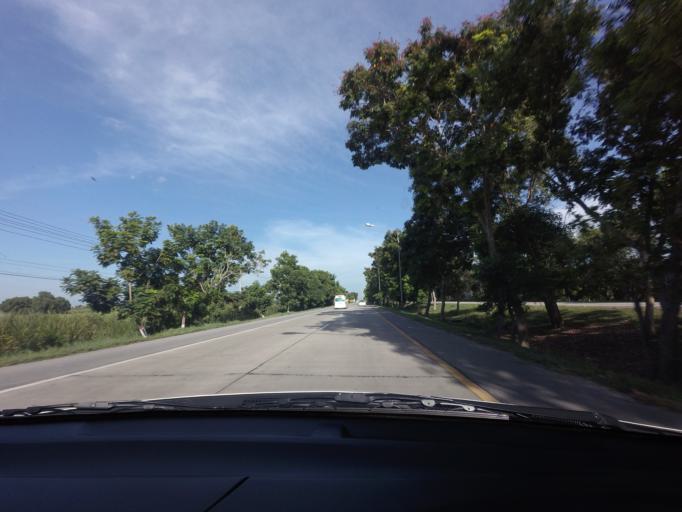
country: TH
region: Suphan Buri
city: Bang Pla Ma
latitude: 14.3319
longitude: 100.2081
